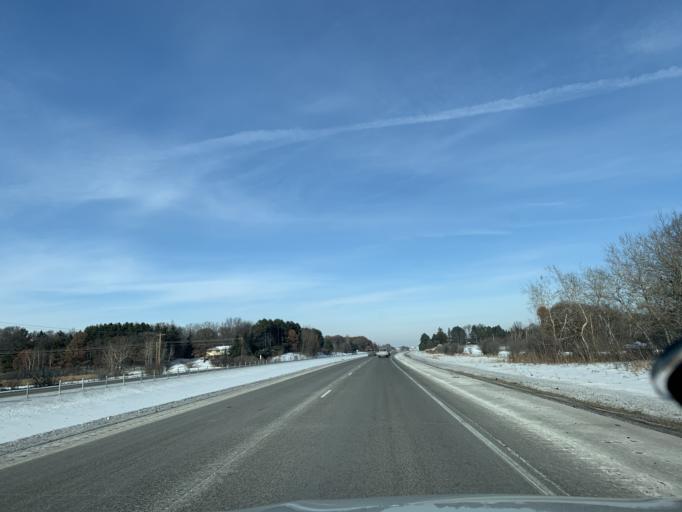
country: US
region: Minnesota
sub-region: Chisago County
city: Wyoming
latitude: 45.3106
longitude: -93.0032
